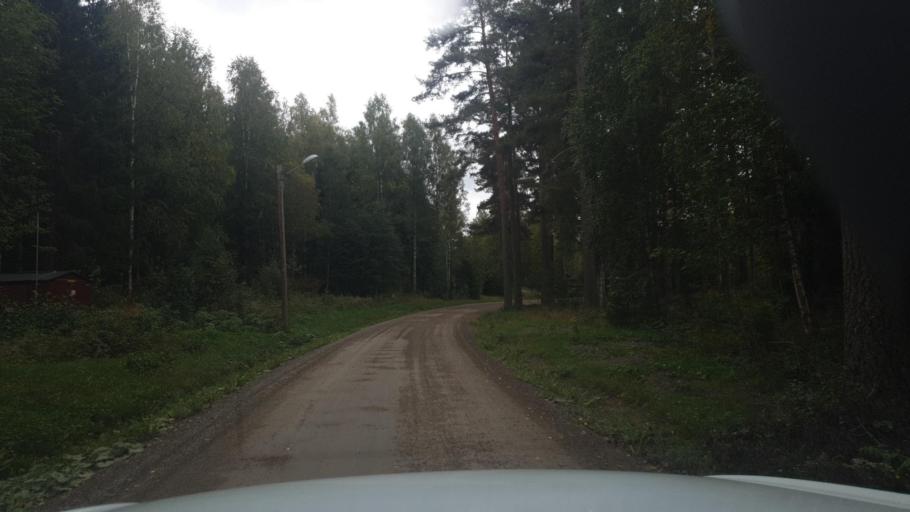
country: SE
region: Vaermland
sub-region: Arvika Kommun
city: Arvika
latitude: 59.9382
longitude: 12.6647
